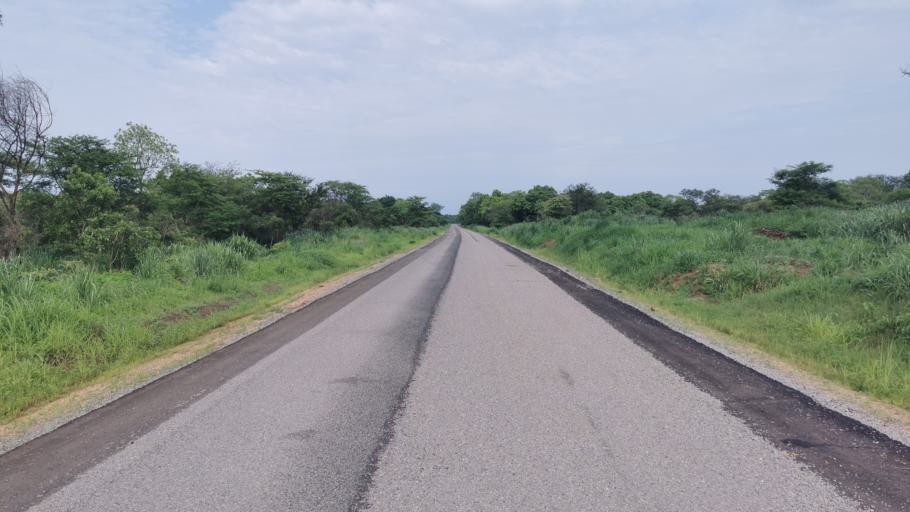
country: ET
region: Gambela
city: Gambela
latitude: 7.8263
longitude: 34.5904
